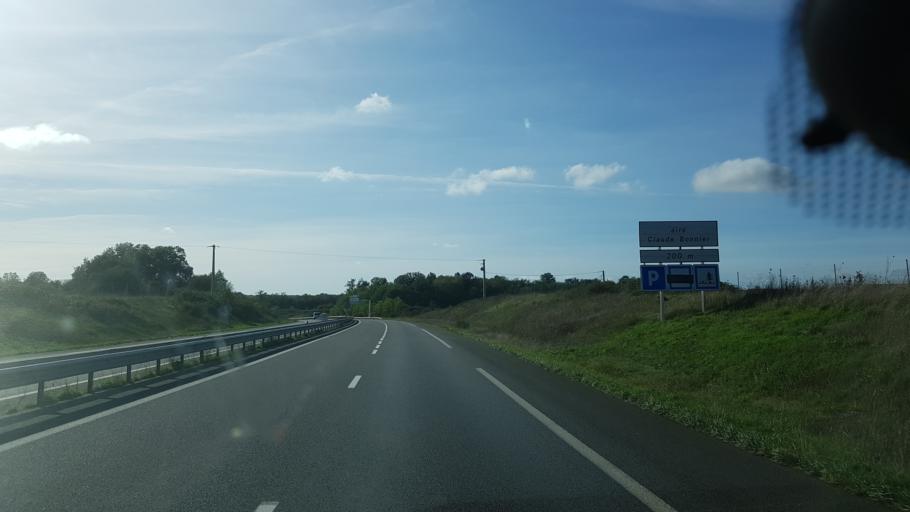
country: FR
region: Poitou-Charentes
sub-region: Departement de la Charente
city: Rivieres
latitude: 45.7403
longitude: 0.3506
